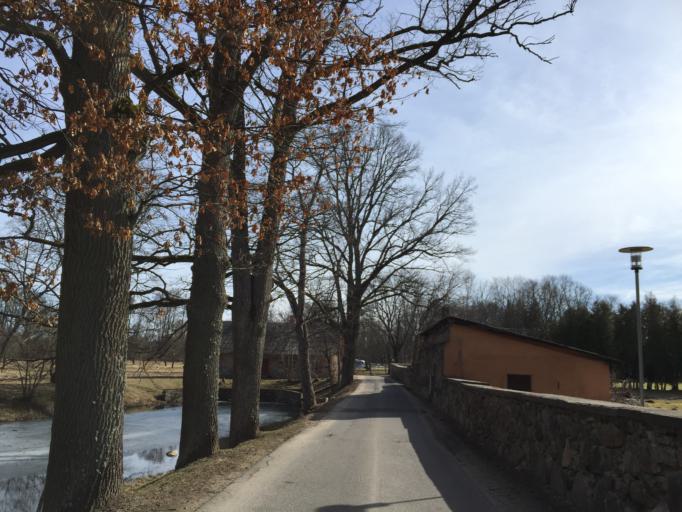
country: LV
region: Sigulda
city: Sigulda
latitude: 57.1657
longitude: 24.8521
